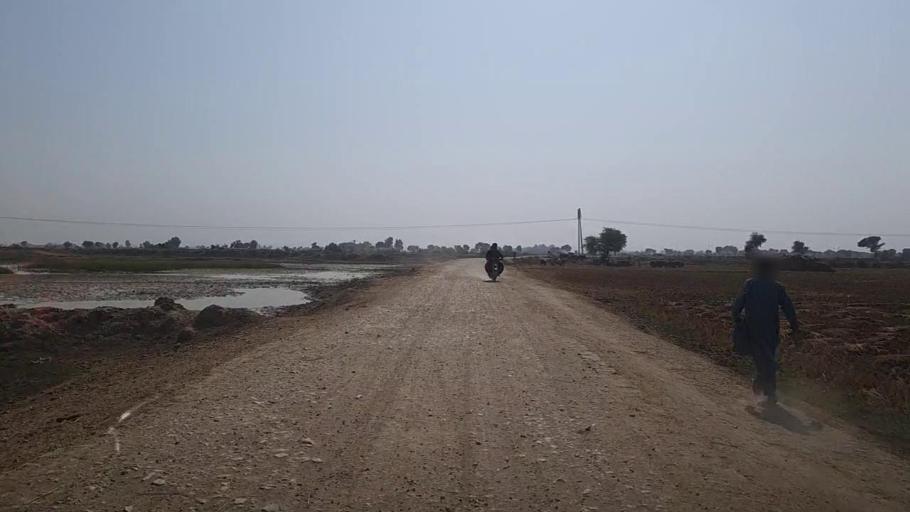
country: PK
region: Sindh
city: Kandhkot
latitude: 28.3898
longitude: 69.2934
